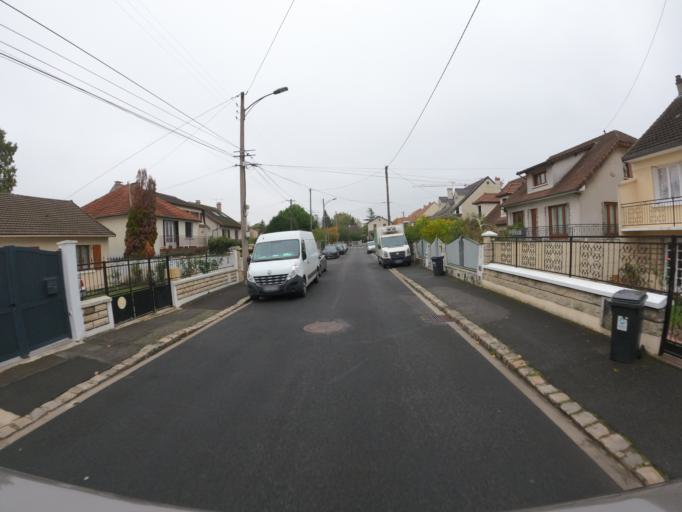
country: FR
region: Ile-de-France
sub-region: Departement du Val-de-Marne
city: Le Plessis-Trevise
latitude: 48.8135
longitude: 2.5645
